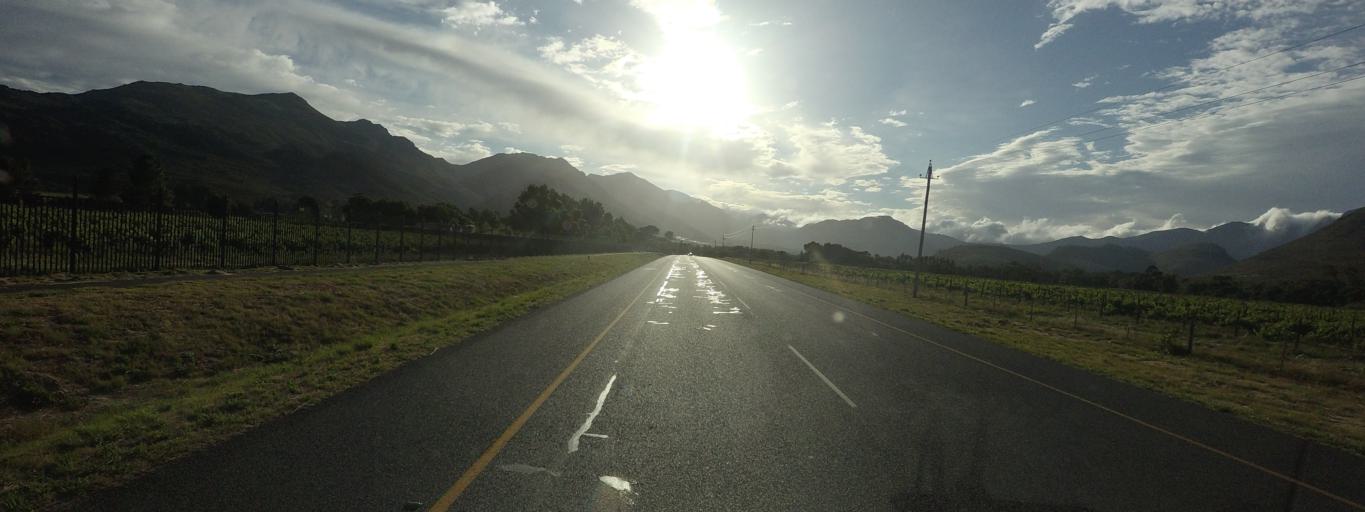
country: ZA
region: Western Cape
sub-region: Cape Winelands District Municipality
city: Paarl
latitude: -33.8795
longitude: 19.0564
